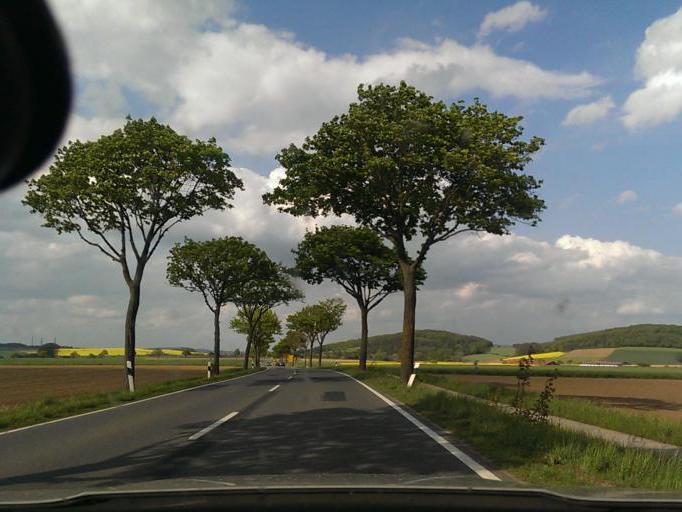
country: DE
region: Lower Saxony
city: Marienhagen
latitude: 52.0500
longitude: 9.6940
